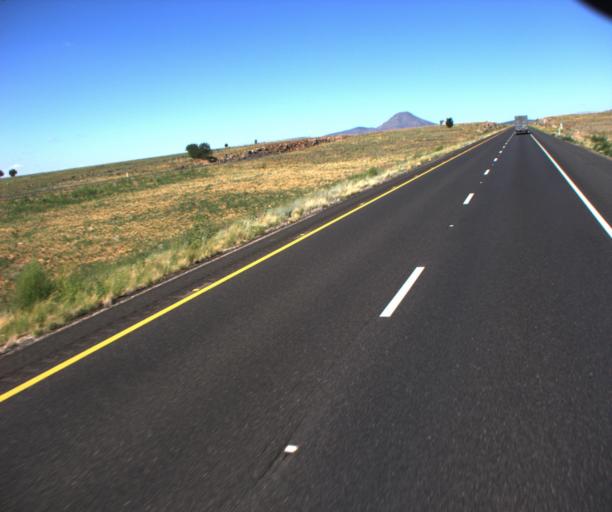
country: US
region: Arizona
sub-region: Yavapai County
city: Paulden
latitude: 35.2336
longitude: -112.6164
